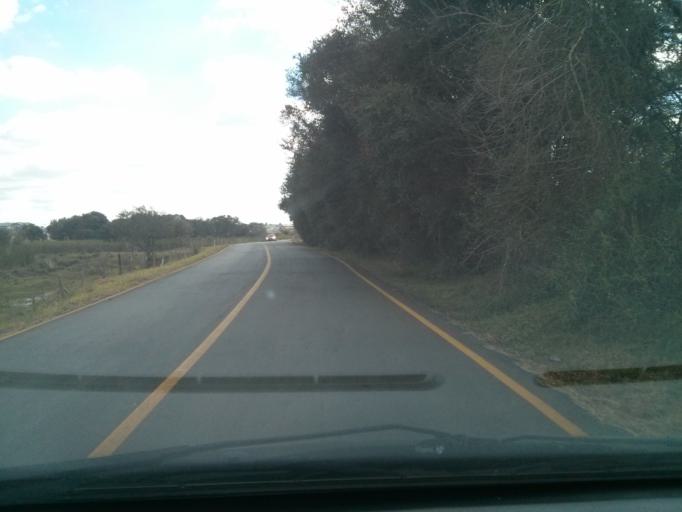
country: BR
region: Parana
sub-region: Sao Jose Dos Pinhais
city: Sao Jose dos Pinhais
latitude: -25.5457
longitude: -49.2246
